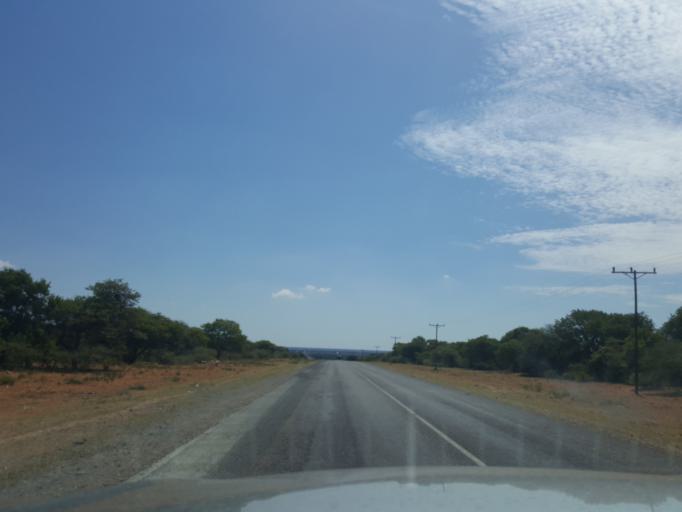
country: BW
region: Kweneng
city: Letlhakeng
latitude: -24.1222
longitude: 25.0873
